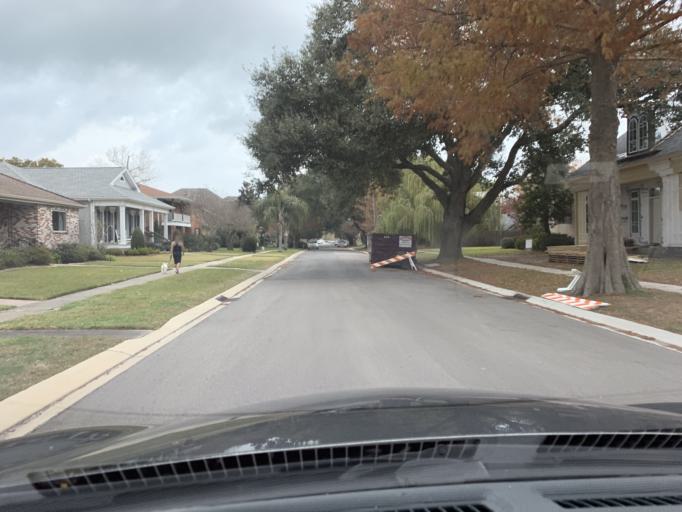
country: US
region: Louisiana
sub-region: Jefferson Parish
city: Metairie
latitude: 30.0081
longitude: -90.1011
